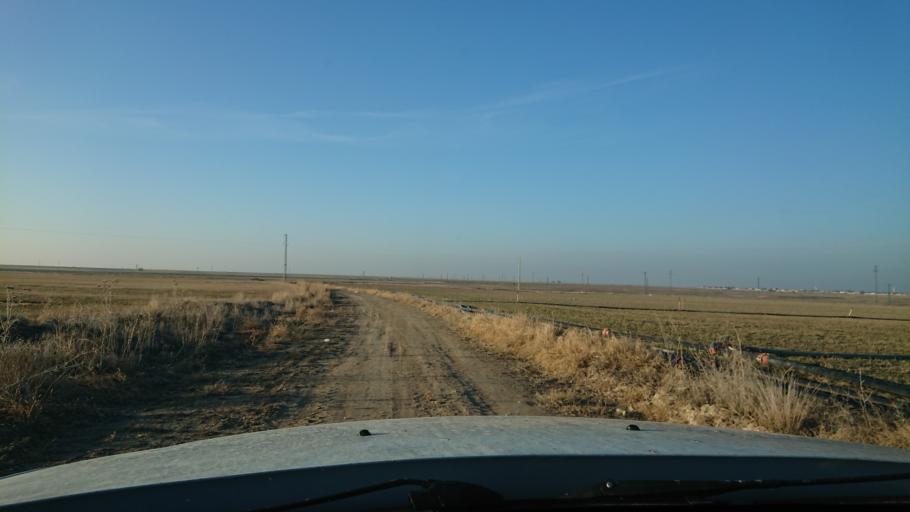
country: TR
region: Aksaray
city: Sultanhani
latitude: 38.2690
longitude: 33.5183
